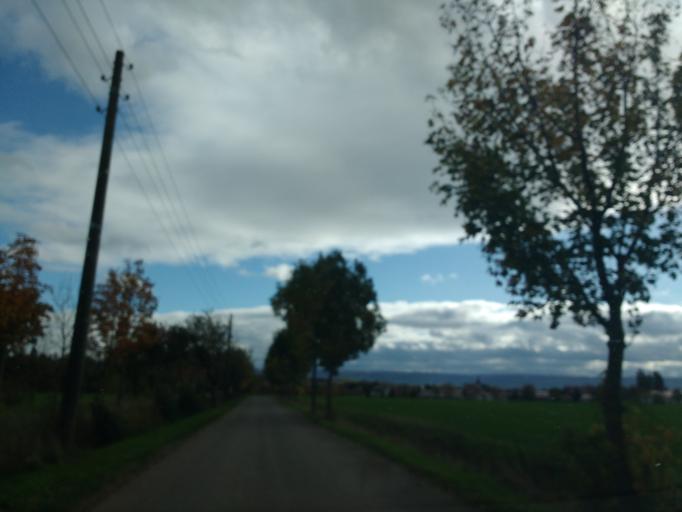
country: DE
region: Thuringia
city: Buhla
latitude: 51.4223
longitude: 10.4240
